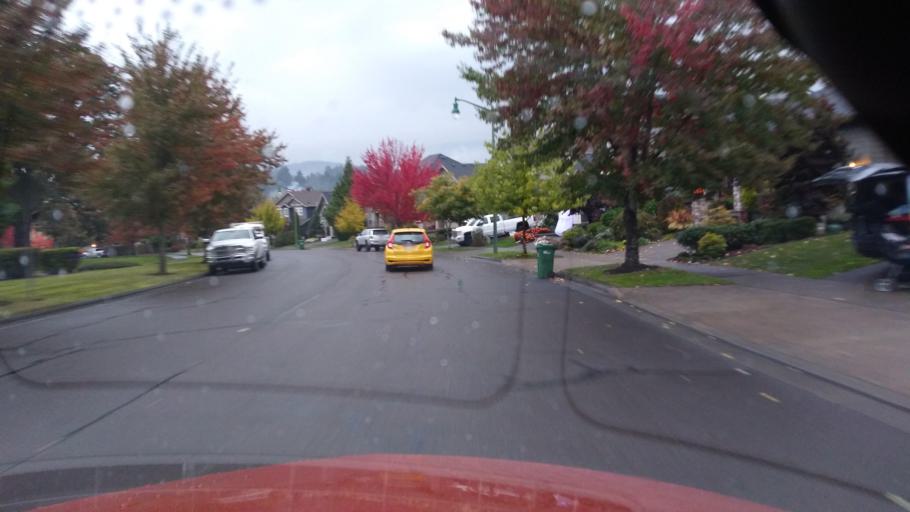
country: US
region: Oregon
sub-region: Washington County
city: Forest Grove
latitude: 45.5259
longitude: -123.1297
